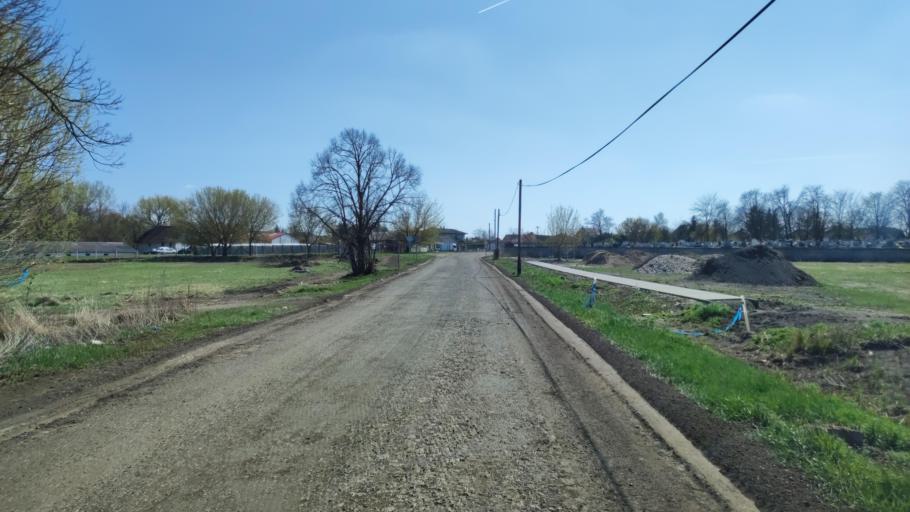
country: HU
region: Pest
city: Szod
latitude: 47.7185
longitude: 19.1919
